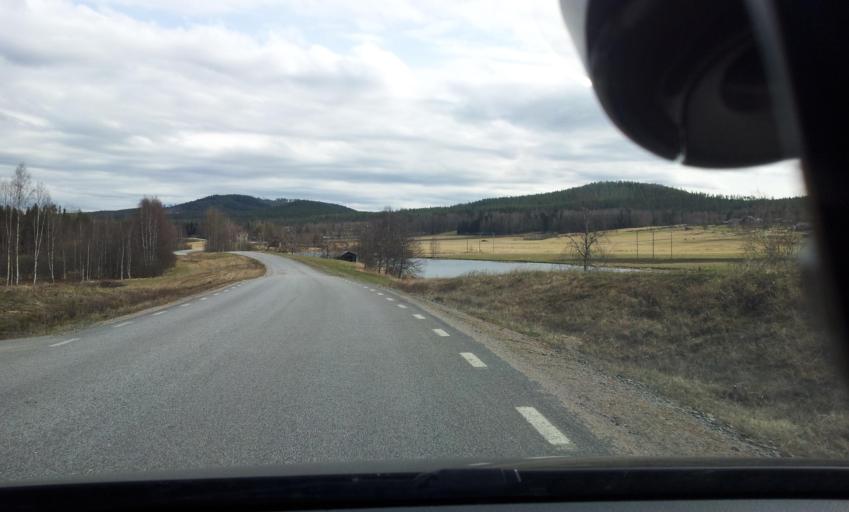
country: SE
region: Gaevleborg
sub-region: Ljusdals Kommun
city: Farila
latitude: 61.7737
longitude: 15.9580
